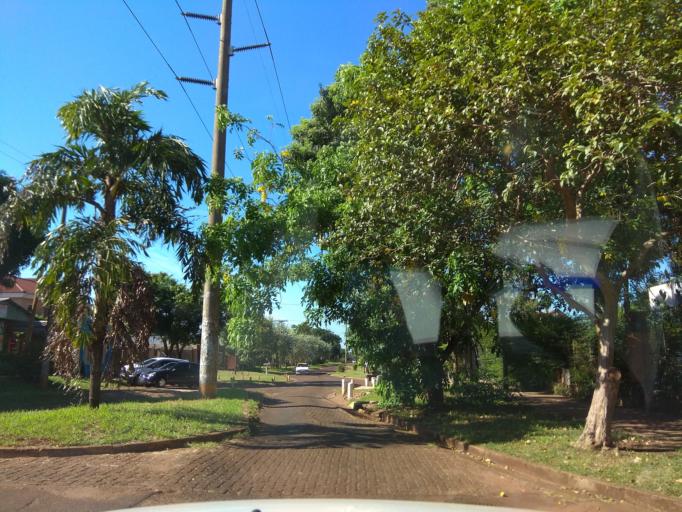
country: AR
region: Misiones
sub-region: Departamento de Capital
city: Posadas
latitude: -27.3928
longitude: -55.9164
